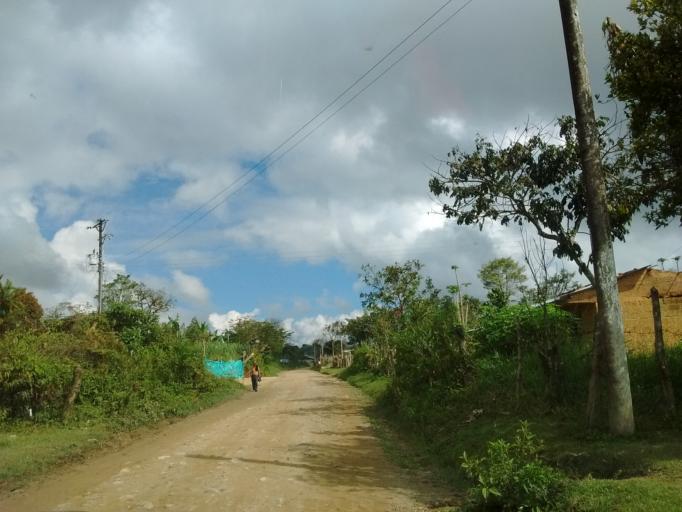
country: CO
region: Cauca
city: Morales
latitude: 2.6610
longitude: -76.6981
